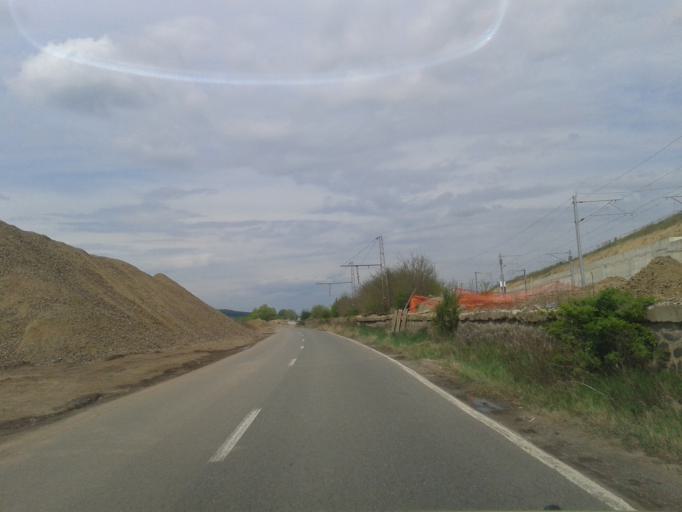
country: RO
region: Alba
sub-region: Comuna Valea Lunga
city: Valea Lunga
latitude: 46.0923
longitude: 24.0640
